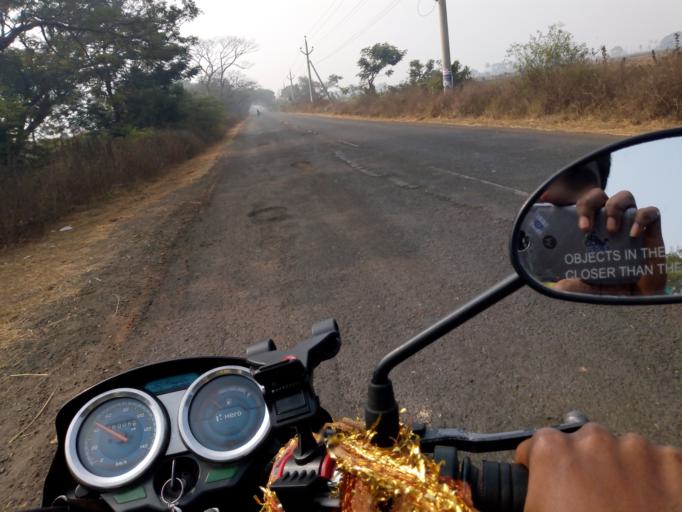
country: IN
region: Andhra Pradesh
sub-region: West Godavari
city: Tadepallegudem
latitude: 16.7512
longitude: 81.4222
